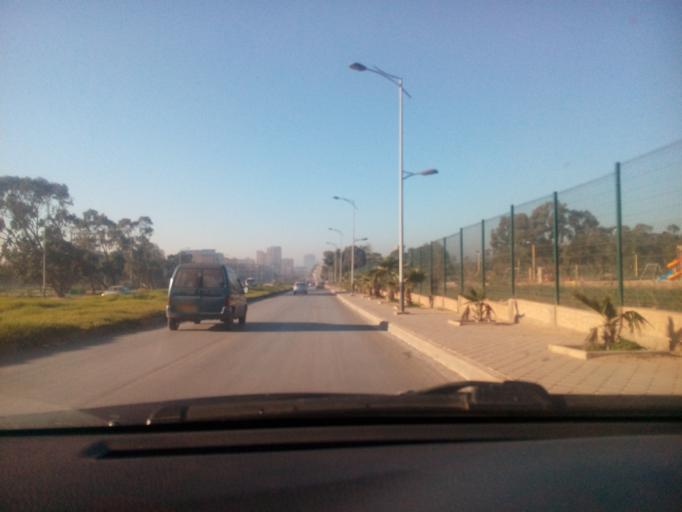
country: DZ
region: Oran
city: Bir el Djir
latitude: 35.7432
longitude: -0.5644
